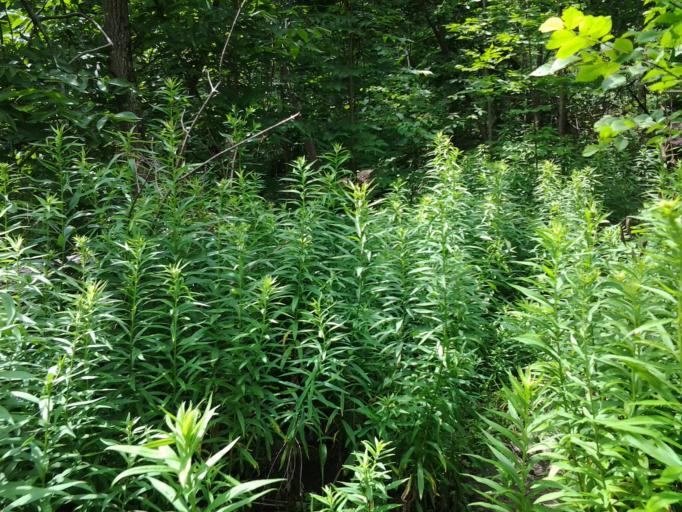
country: CA
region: Ontario
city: Orangeville
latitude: 43.7969
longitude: -80.0069
